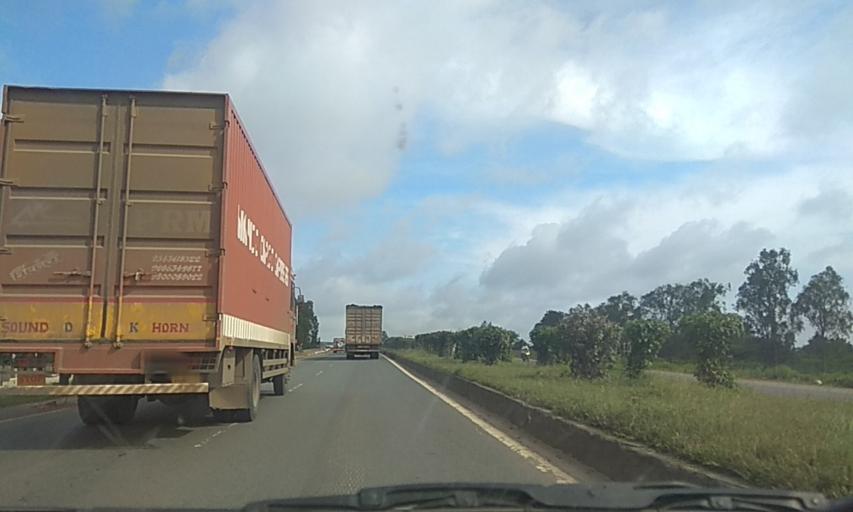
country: IN
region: Karnataka
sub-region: Haveri
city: Shiggaon
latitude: 15.0219
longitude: 75.1825
